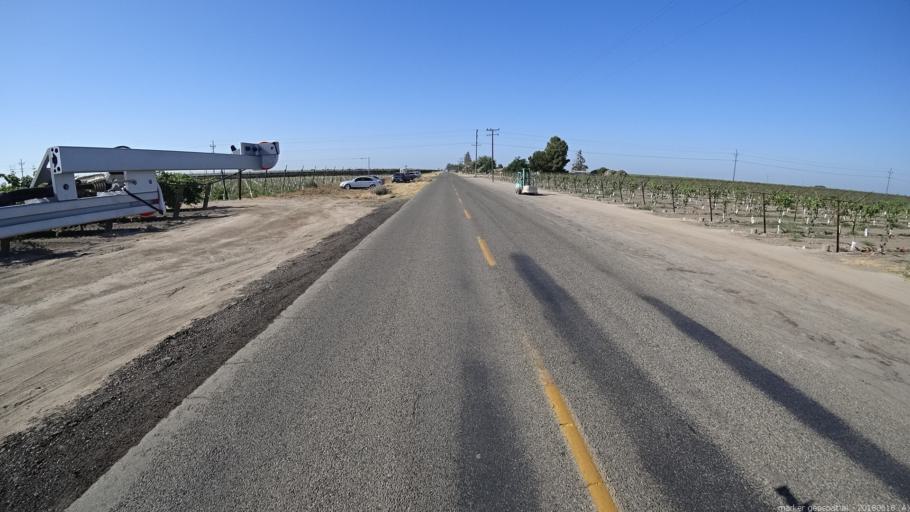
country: US
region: California
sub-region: Madera County
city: Parkwood
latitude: 36.8814
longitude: -120.1285
